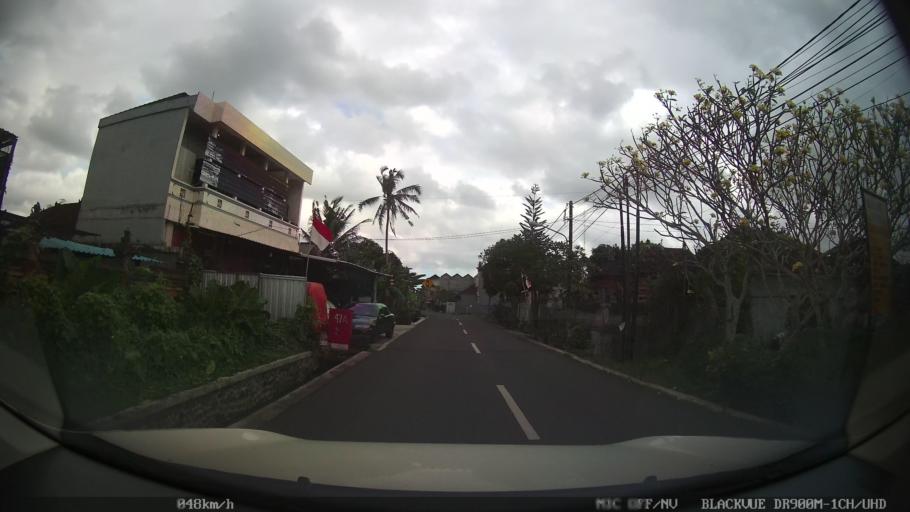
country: ID
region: Bali
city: Banjar Tegal Belodan
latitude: -8.5437
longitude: 115.1158
